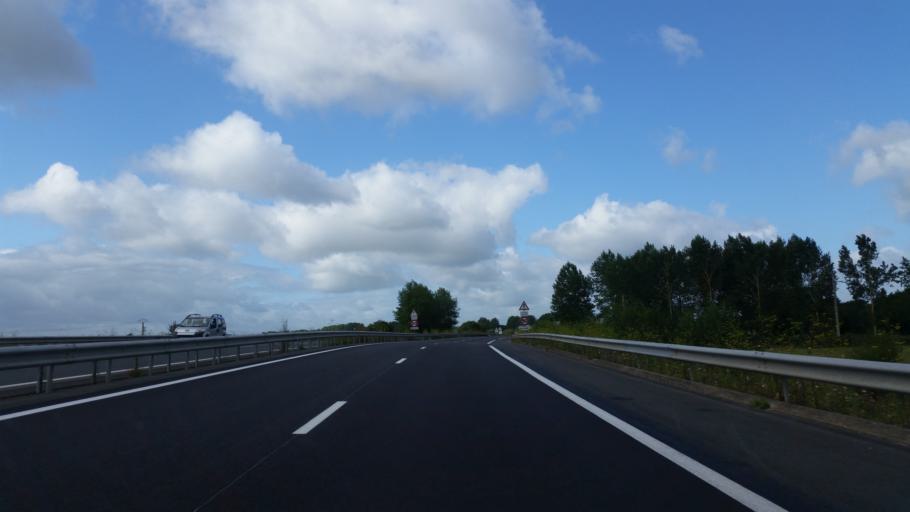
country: FR
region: Lower Normandy
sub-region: Departement du Calvados
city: Isigny-sur-Mer
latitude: 49.3261
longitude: -1.0808
